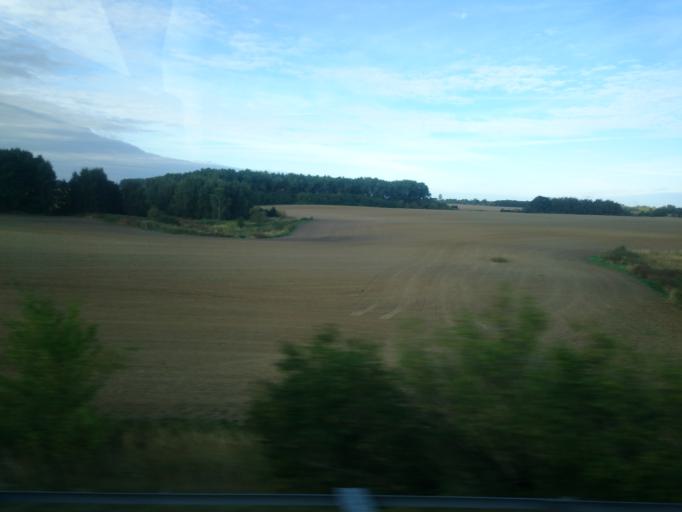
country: DE
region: Mecklenburg-Vorpommern
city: Anklam
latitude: 53.8336
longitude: 13.7171
